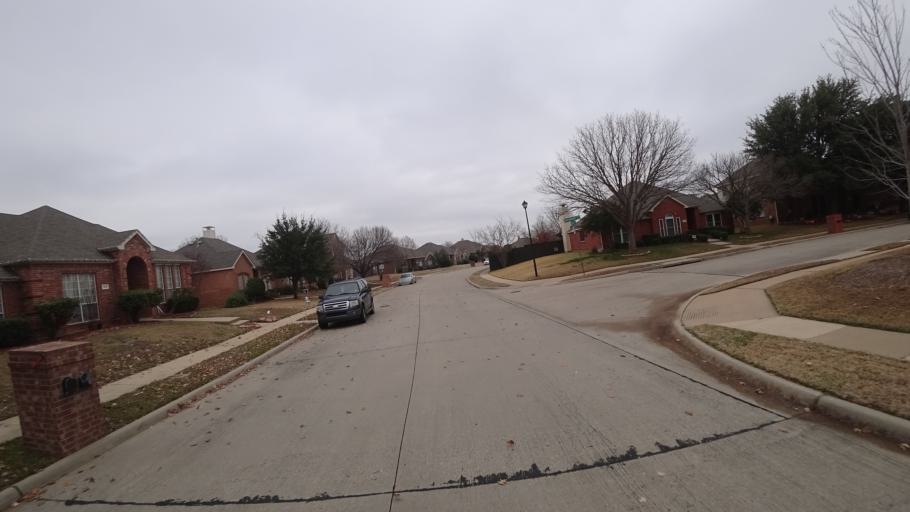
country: US
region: Texas
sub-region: Denton County
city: Highland Village
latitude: 33.0590
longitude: -97.0324
